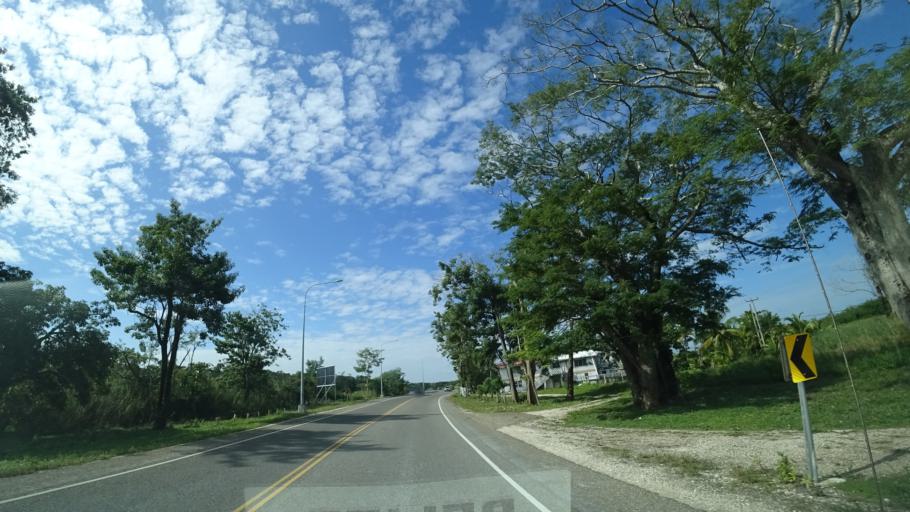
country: BZ
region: Belize
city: Belize City
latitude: 17.5461
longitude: -88.2800
